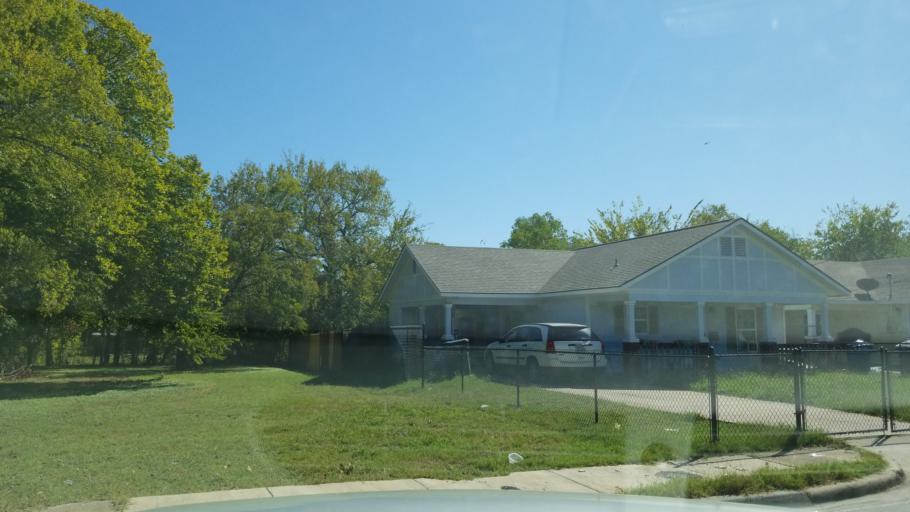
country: US
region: Texas
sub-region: Dallas County
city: Dallas
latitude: 32.7792
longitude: -96.7464
